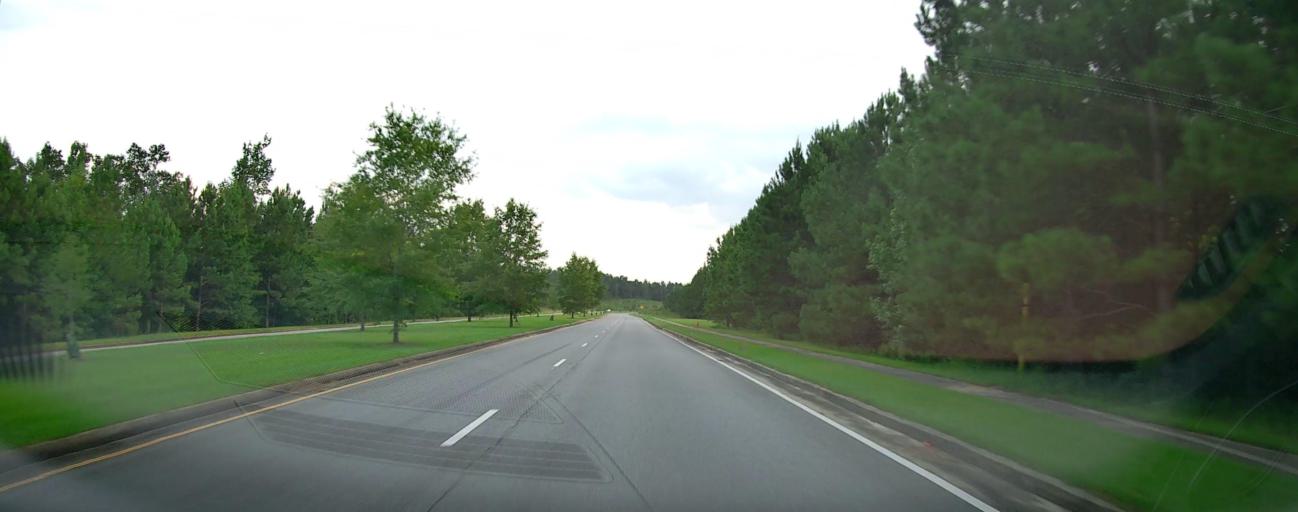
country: US
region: Georgia
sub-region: Muscogee County
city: Columbus
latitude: 32.5182
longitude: -84.8446
